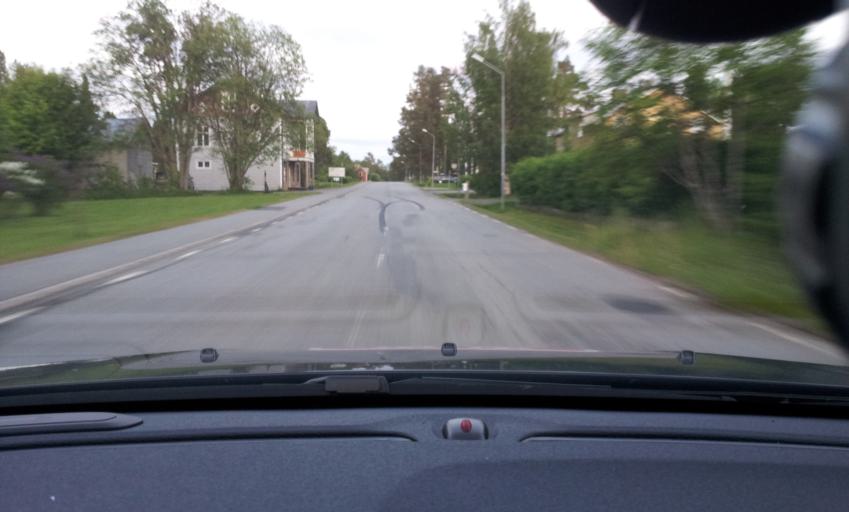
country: SE
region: Jaemtland
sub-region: Ragunda Kommun
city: Hammarstrand
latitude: 62.9760
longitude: 16.0892
